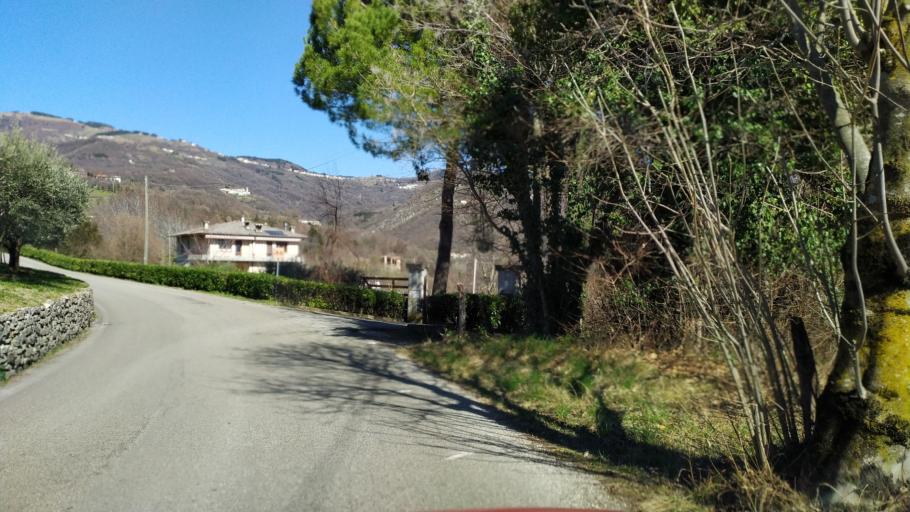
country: IT
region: Veneto
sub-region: Provincia di Vicenza
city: Fara Vicentino
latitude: 45.7568
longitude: 11.5421
